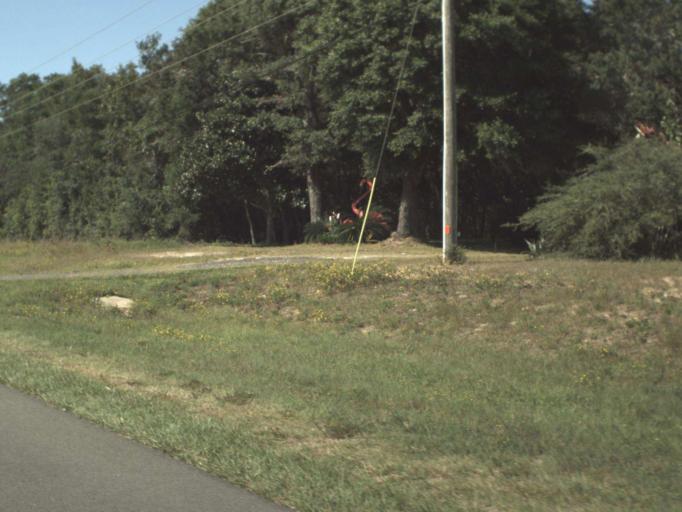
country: US
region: Florida
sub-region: Walton County
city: Miramar Beach
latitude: 30.4659
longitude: -86.3566
